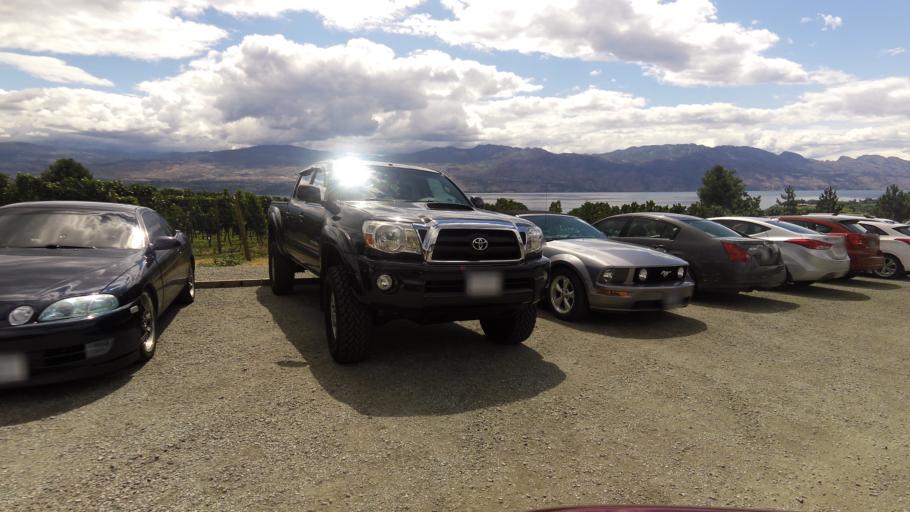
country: CA
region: British Columbia
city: West Kelowna
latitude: 49.8423
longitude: -119.5673
